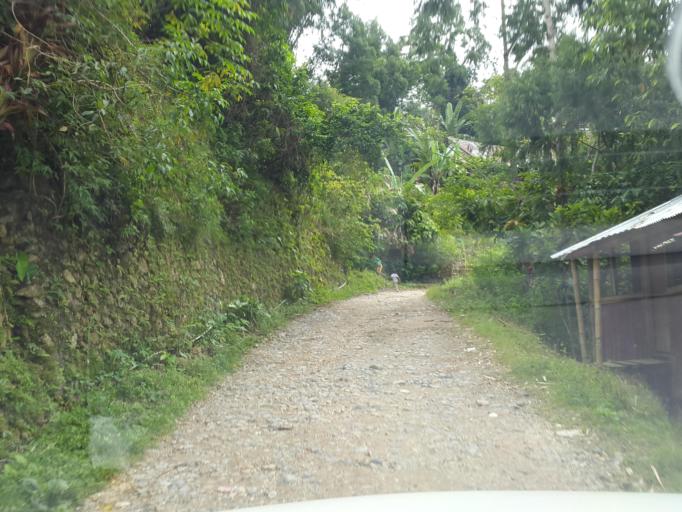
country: ID
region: South Sulawesi
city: Rantepang
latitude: -2.8685
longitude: 119.9476
